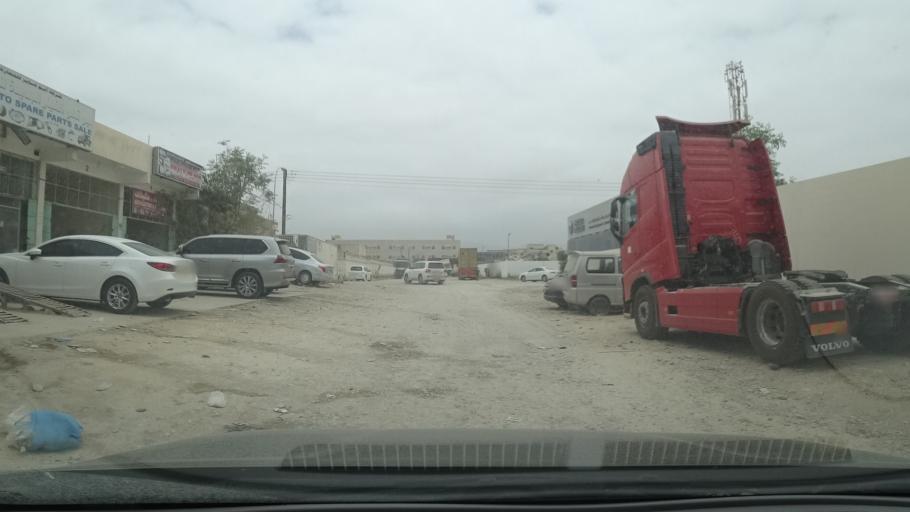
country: OM
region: Zufar
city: Salalah
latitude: 17.0215
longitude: 54.0543
